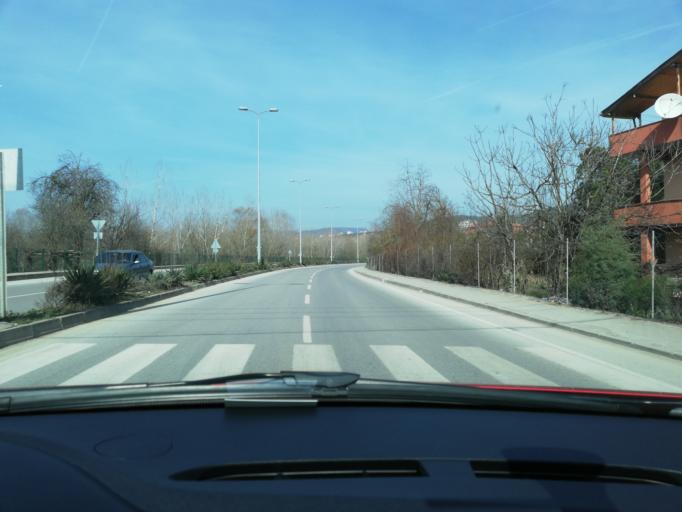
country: TR
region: Bartin
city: Bartin
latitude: 41.6318
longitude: 32.3495
